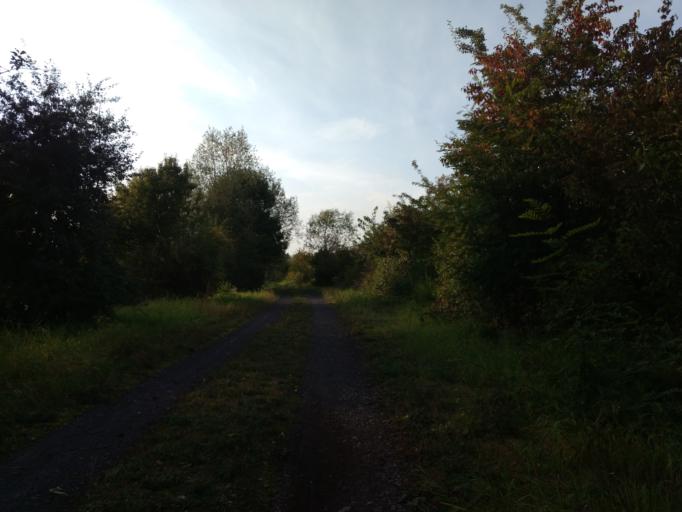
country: DE
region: Saarland
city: Saarlouis
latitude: 49.3210
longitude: 6.7717
